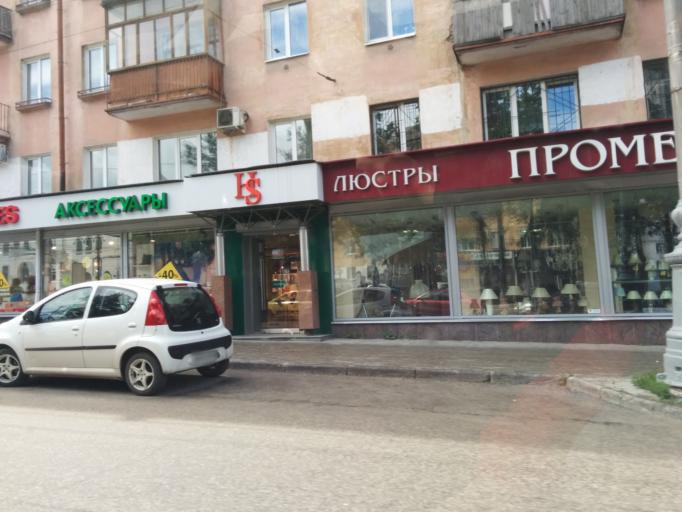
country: RU
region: Perm
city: Perm
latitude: 58.0067
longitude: 56.2428
